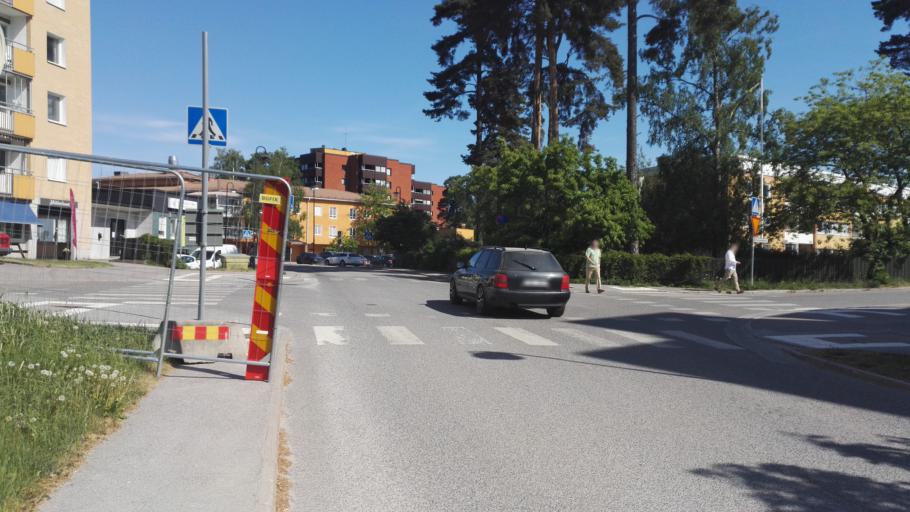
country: SE
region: Stockholm
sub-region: Upplands-Bro Kommun
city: Kungsaengen
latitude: 59.4779
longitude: 17.7487
